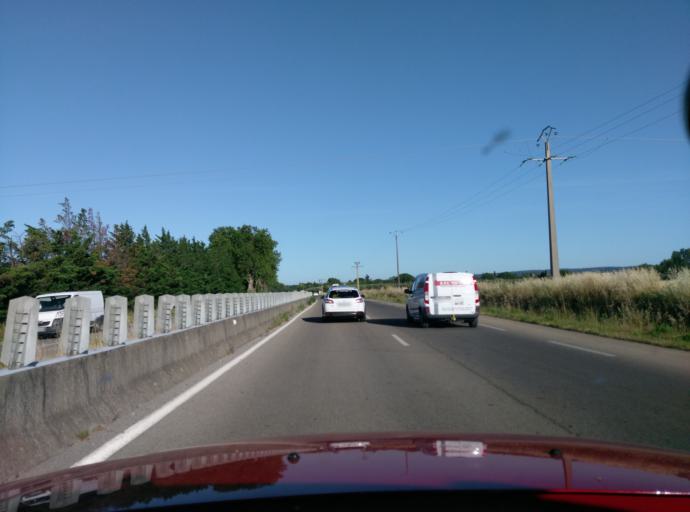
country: FR
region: Languedoc-Roussillon
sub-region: Departement du Gard
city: Rodilhan
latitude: 43.8308
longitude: 4.4492
